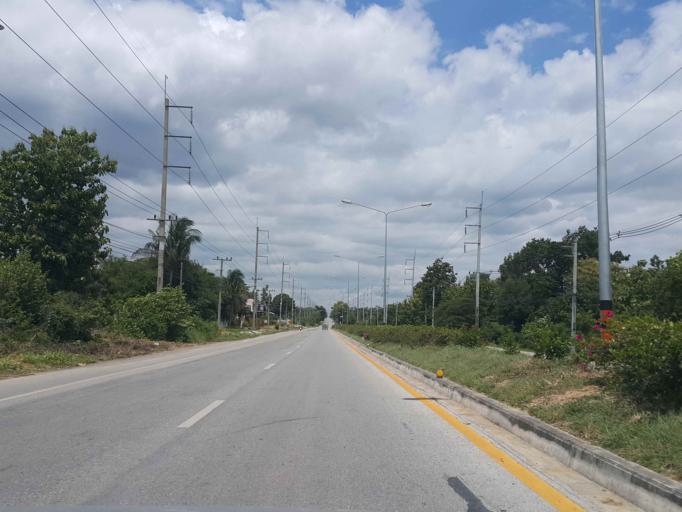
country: TH
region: Lamphun
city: Ban Hong
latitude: 18.3584
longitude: 98.8102
